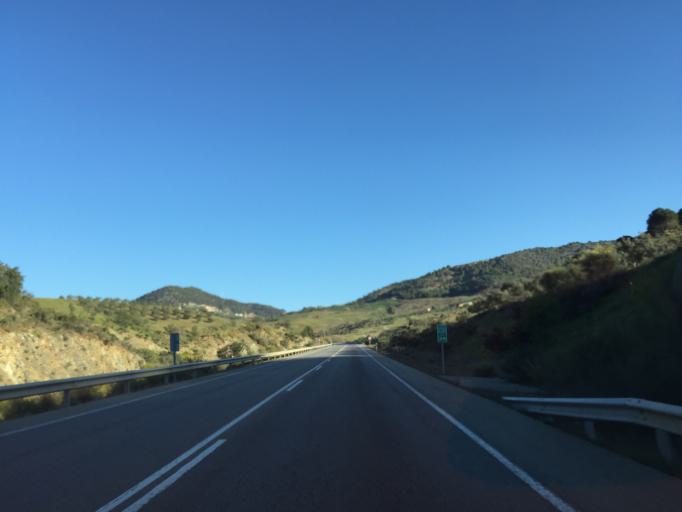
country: ES
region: Andalusia
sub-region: Provincia de Malaga
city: Carratraca
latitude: 36.8350
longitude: -4.8078
